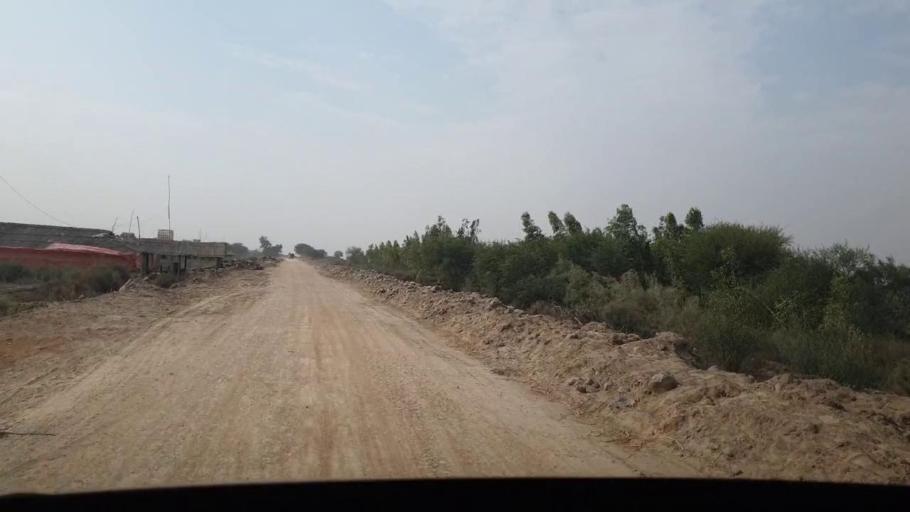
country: PK
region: Sindh
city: Chuhar Jamali
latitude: 24.3660
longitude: 67.9399
